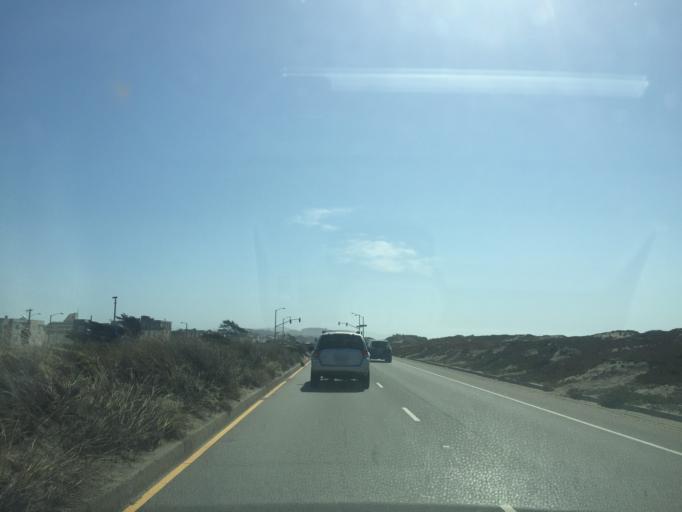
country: US
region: California
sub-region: San Mateo County
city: Daly City
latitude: 37.7432
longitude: -122.5077
